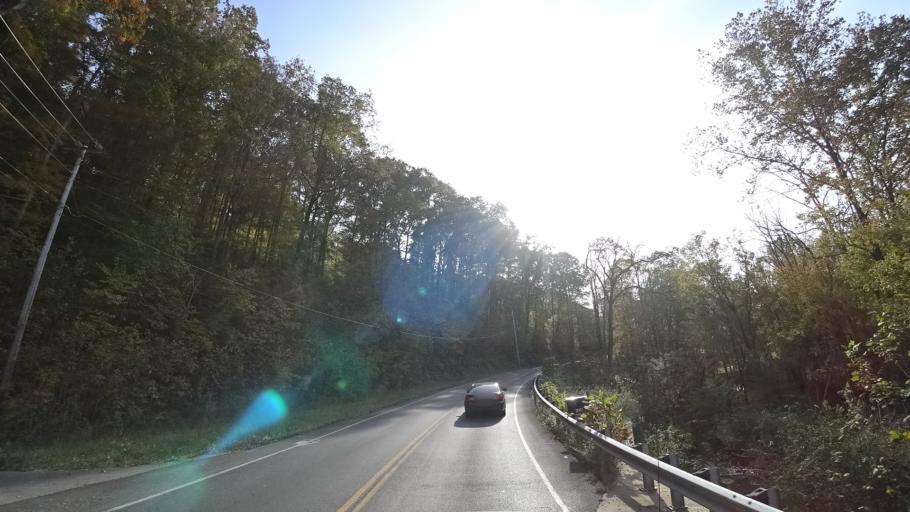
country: US
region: Tennessee
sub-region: Knox County
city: Farragut
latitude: 35.9091
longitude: -84.1861
